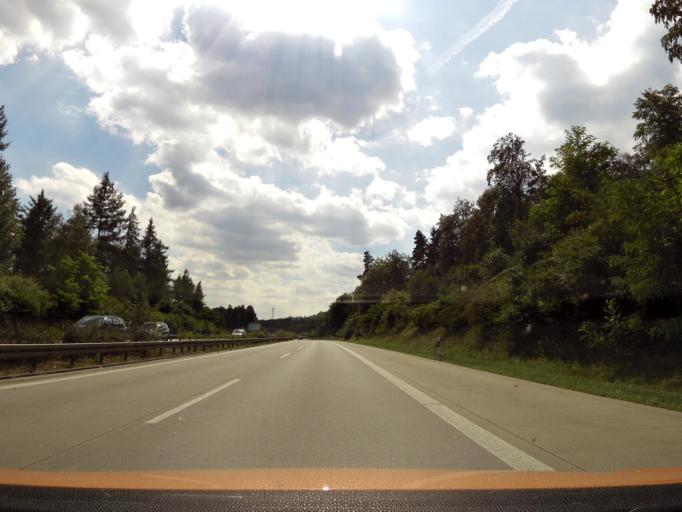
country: DE
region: Brandenburg
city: Wandlitz
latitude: 52.7566
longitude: 13.5443
